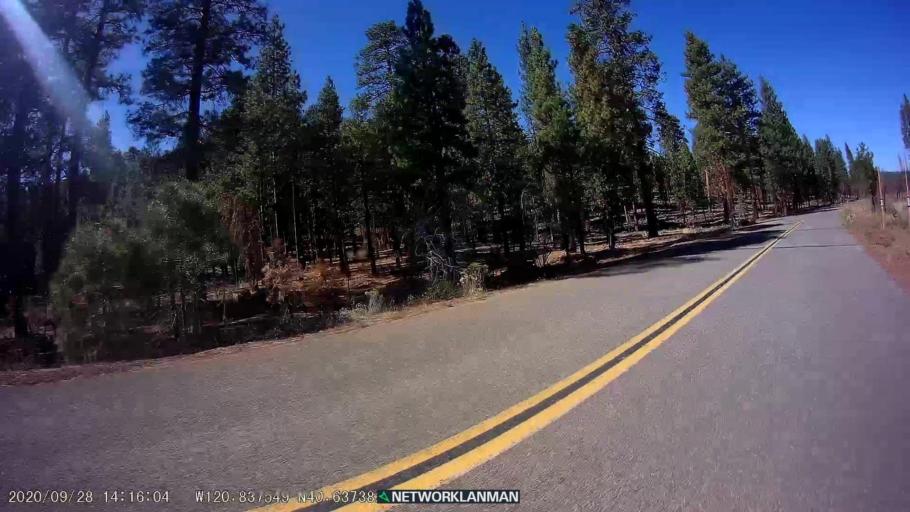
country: US
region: California
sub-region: Lassen County
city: Susanville
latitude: 40.6378
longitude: -120.8376
